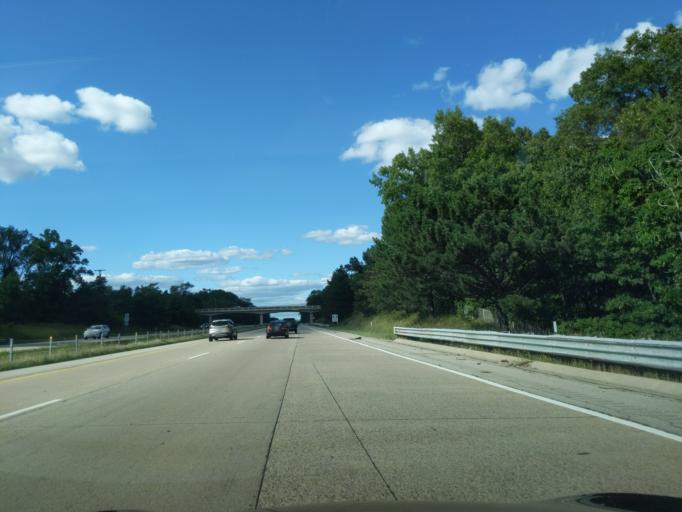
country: US
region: Michigan
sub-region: Muskegon County
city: Muskegon Heights
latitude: 43.1778
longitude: -86.2050
